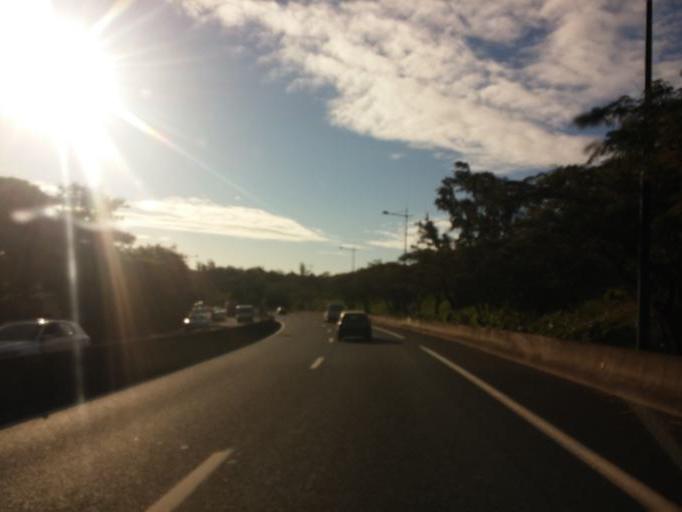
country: RE
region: Reunion
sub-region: Reunion
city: Saint-Denis
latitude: -20.8872
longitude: 55.5001
